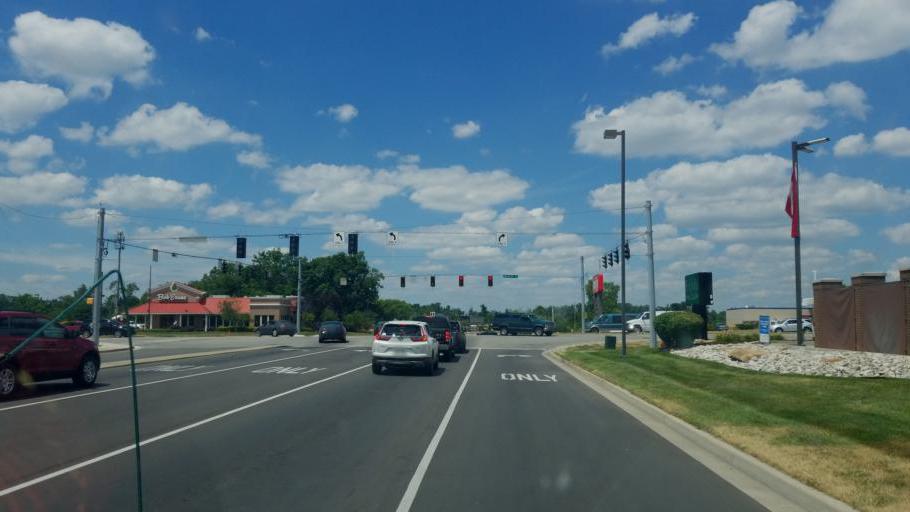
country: US
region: Indiana
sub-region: Allen County
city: New Haven
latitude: 41.1292
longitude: -85.0110
